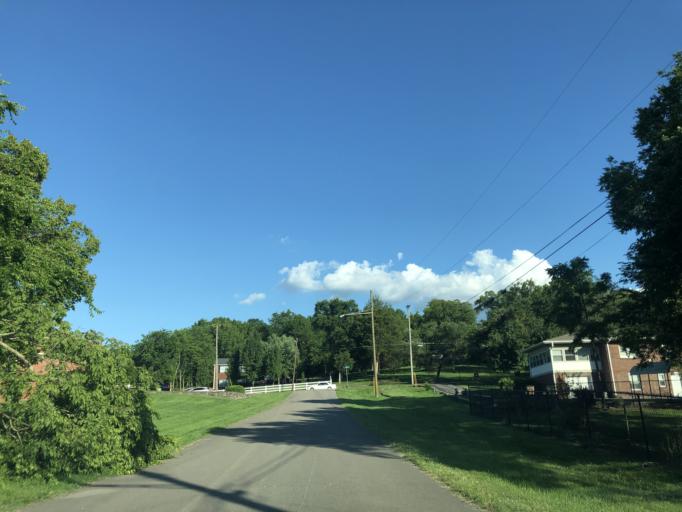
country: US
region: Tennessee
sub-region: Davidson County
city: Nashville
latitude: 36.2007
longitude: -86.8499
